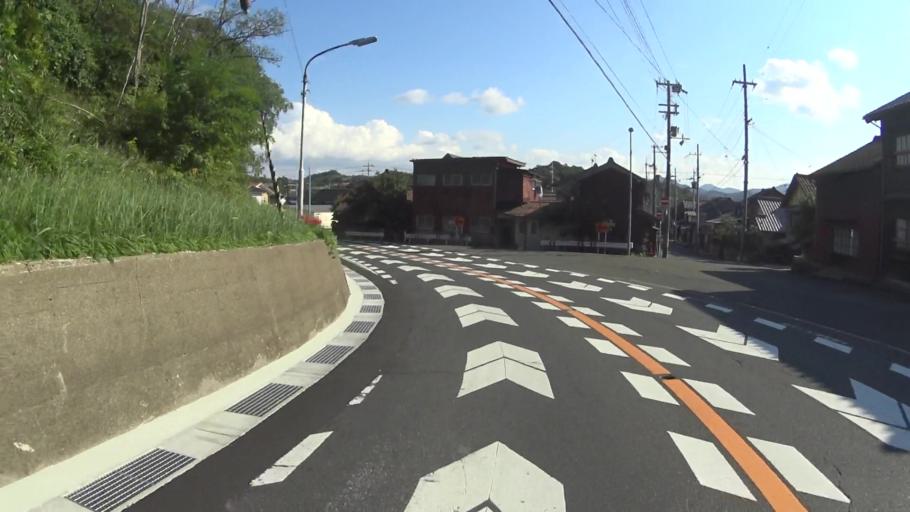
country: JP
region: Kyoto
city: Miyazu
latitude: 35.6831
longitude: 135.0301
